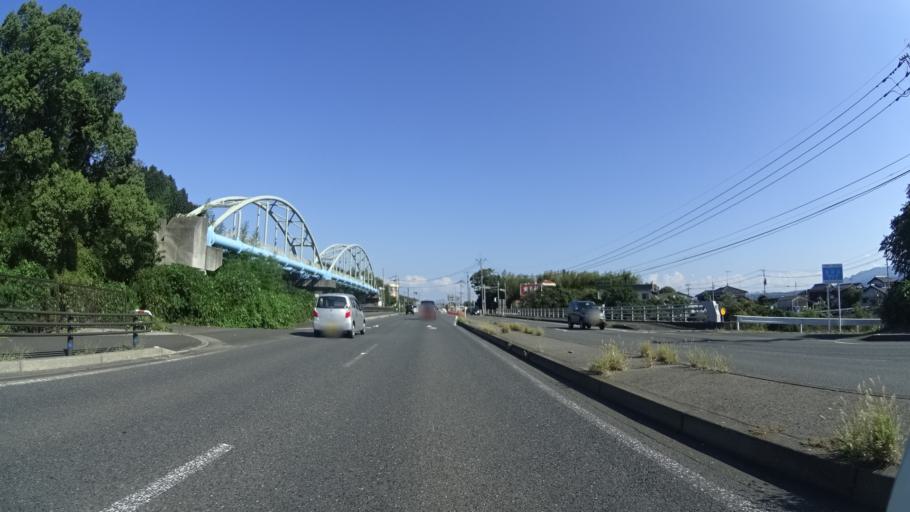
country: JP
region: Fukuoka
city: Yoshitomi
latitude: 33.5908
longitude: 131.1510
